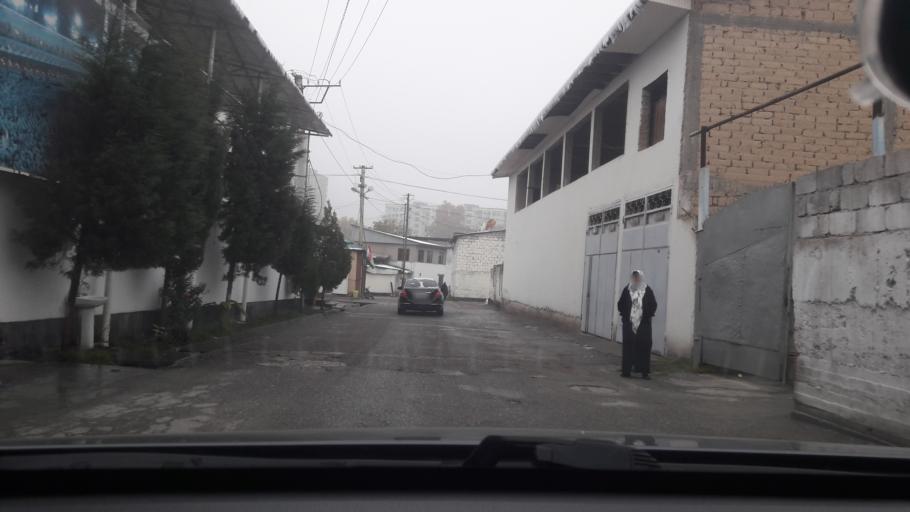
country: TJ
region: Dushanbe
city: Dushanbe
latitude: 38.5895
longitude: 68.7473
